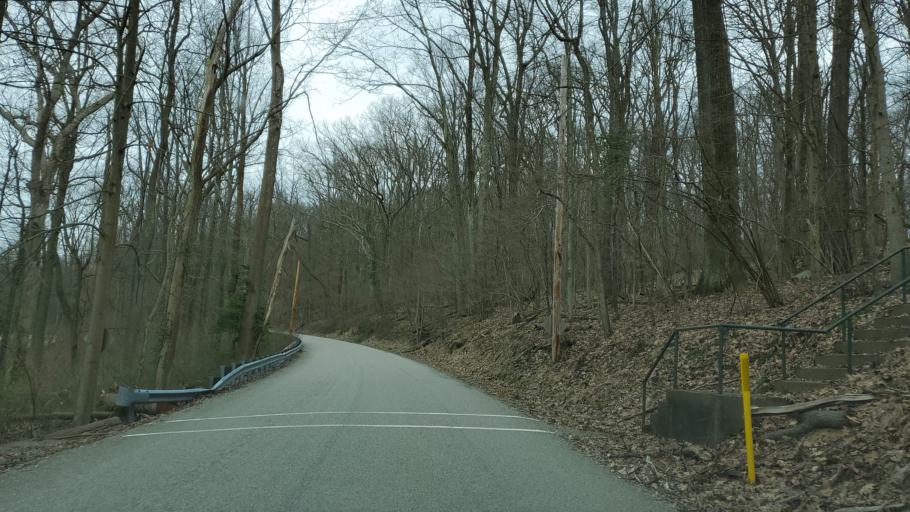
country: US
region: Pennsylvania
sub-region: Westmoreland County
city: Ligonier
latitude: 40.1838
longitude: -79.2401
